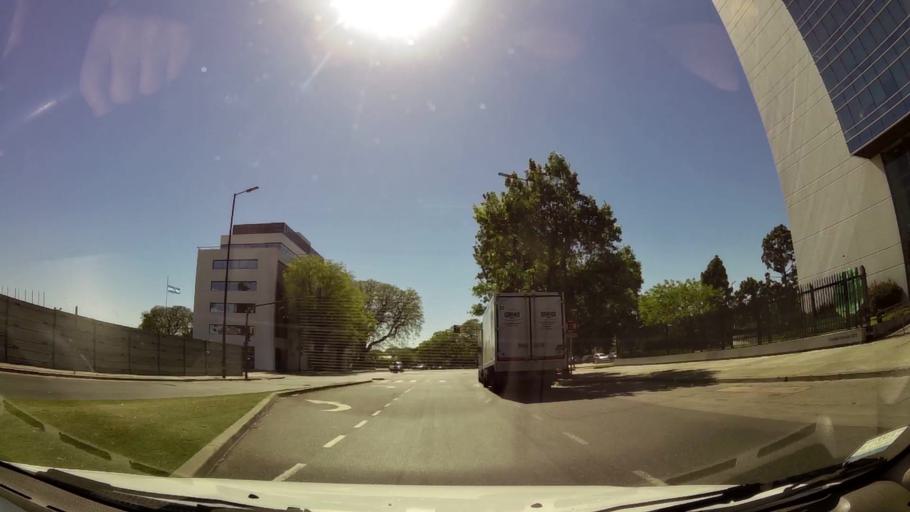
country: AR
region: Buenos Aires F.D.
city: Buenos Aires
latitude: -34.5984
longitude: -58.3649
